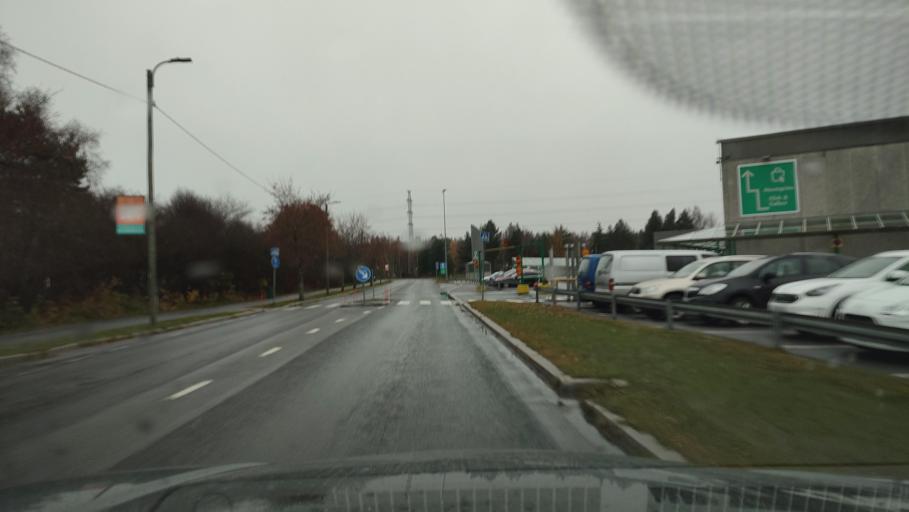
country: FI
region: Ostrobothnia
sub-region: Vaasa
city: Vaasa
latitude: 63.1031
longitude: 21.6479
